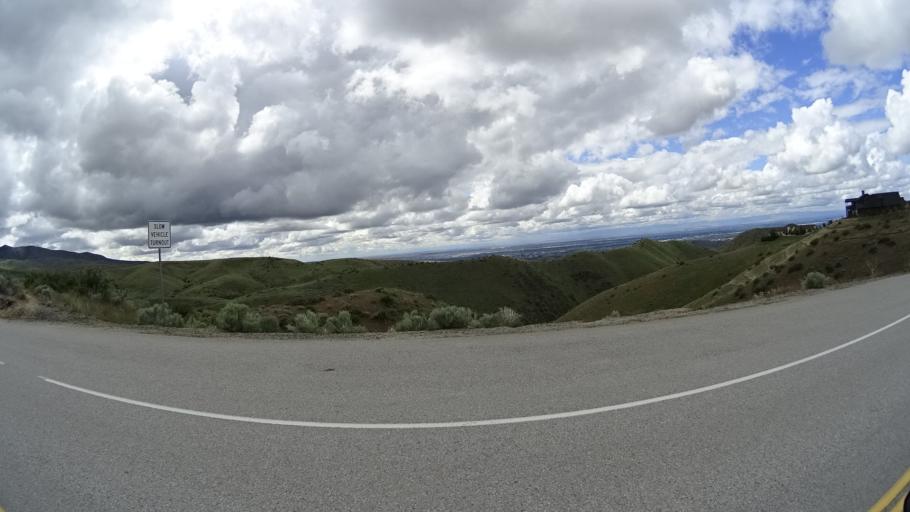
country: US
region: Idaho
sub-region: Ada County
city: Boise
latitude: 43.6935
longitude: -116.1720
